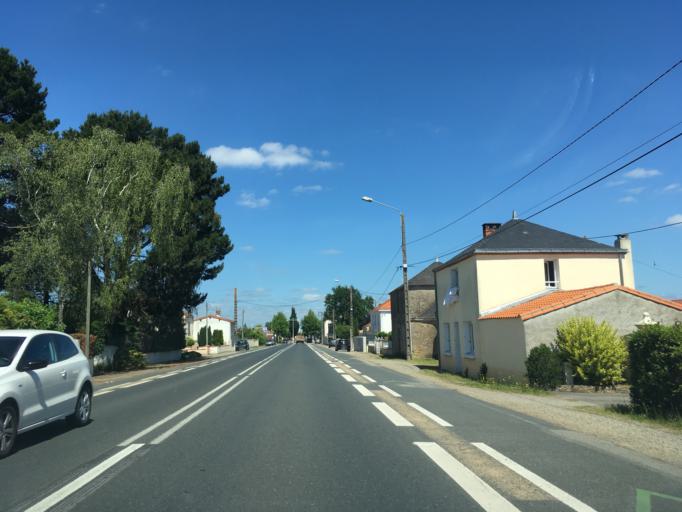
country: FR
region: Pays de la Loire
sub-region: Departement de la Loire-Atlantique
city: Les Sorinieres
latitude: 47.1442
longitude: -1.5260
